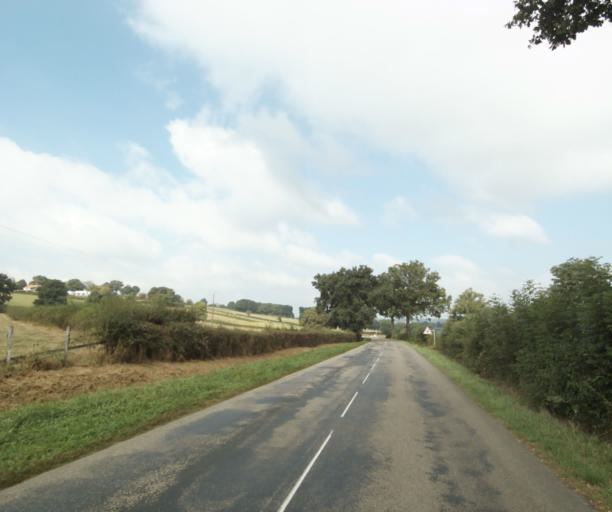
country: FR
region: Bourgogne
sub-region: Departement de Saone-et-Loire
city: Charolles
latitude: 46.4222
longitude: 4.3106
